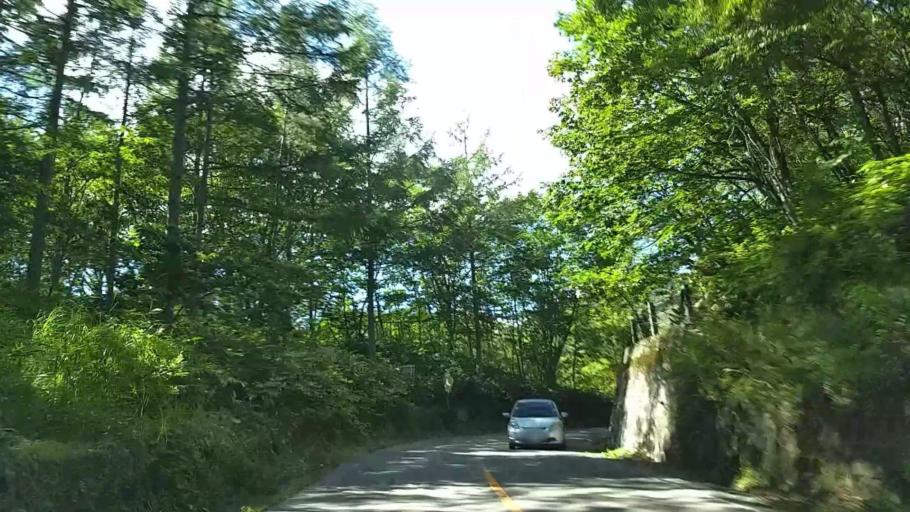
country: JP
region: Nagano
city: Chino
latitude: 36.0807
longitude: 138.2921
